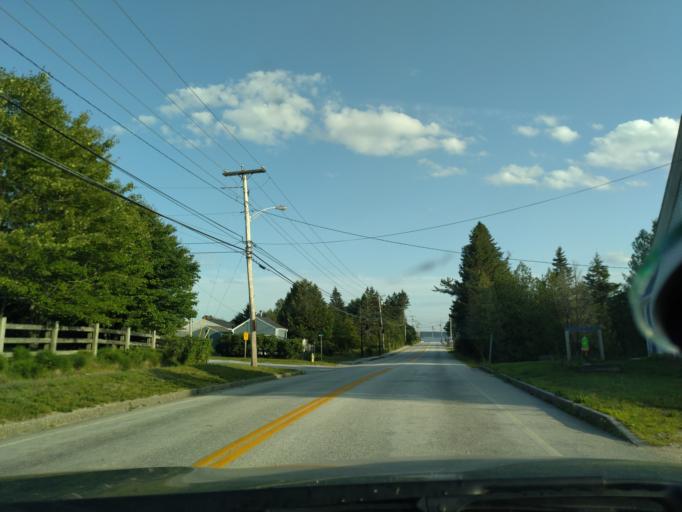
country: US
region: Maine
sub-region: Hancock County
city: Gouldsboro
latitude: 44.3981
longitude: -68.0852
